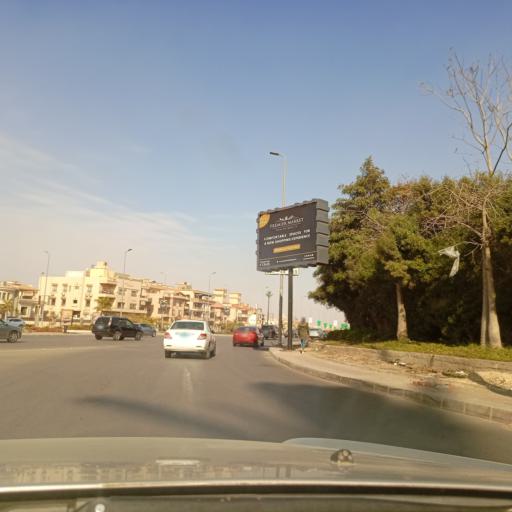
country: EG
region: Muhafazat al Qahirah
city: Cairo
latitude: 30.0214
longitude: 31.4366
